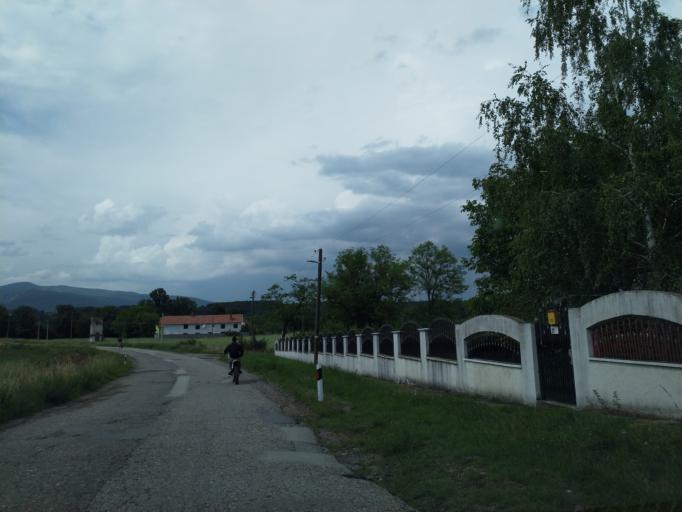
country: RS
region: Central Serbia
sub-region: Zajecarski Okrug
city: Boljevac
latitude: 43.8916
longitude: 21.9670
